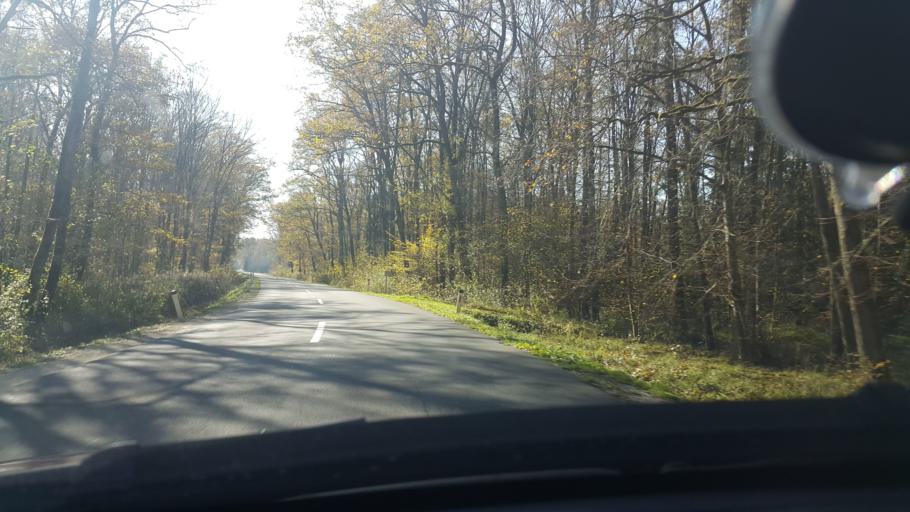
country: SI
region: Brezice
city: Brezice
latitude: 45.9330
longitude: 15.6412
